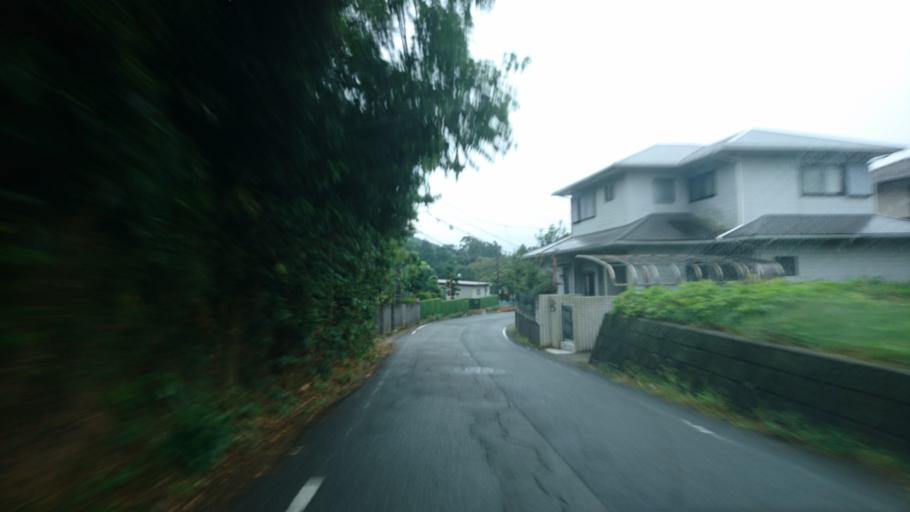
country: JP
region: Chiba
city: Kimitsu
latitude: 35.3311
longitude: 139.9277
